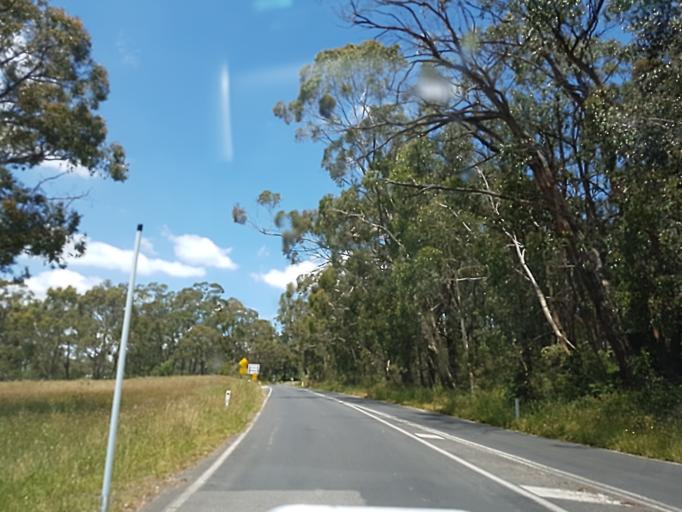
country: AU
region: Victoria
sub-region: Bass Coast
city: North Wonthaggi
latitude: -38.5775
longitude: 145.9824
